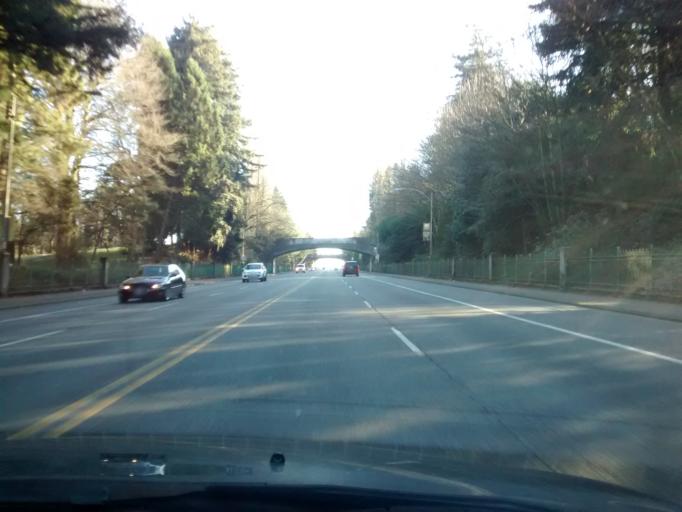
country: US
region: Washington
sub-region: King County
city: Seattle
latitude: 47.6697
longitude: -122.3473
